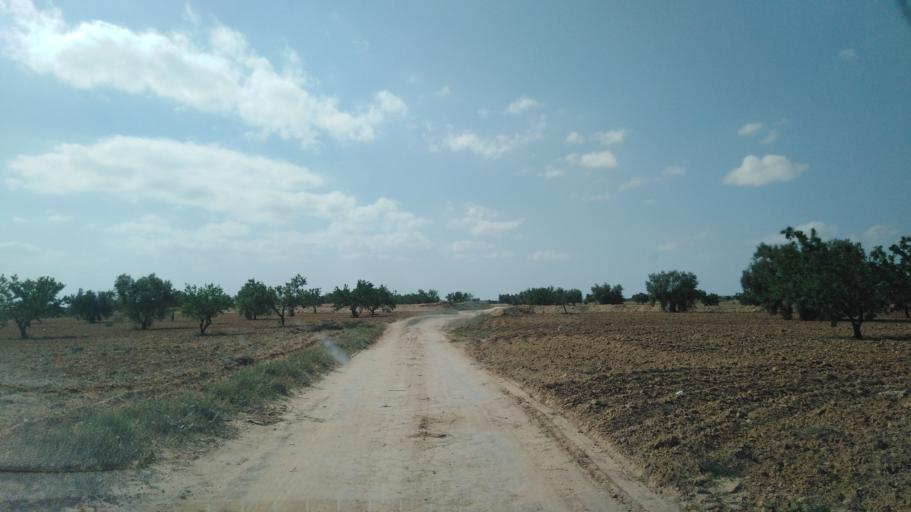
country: TN
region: Safaqis
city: Bi'r `Ali Bin Khalifah
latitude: 34.7957
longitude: 10.3924
